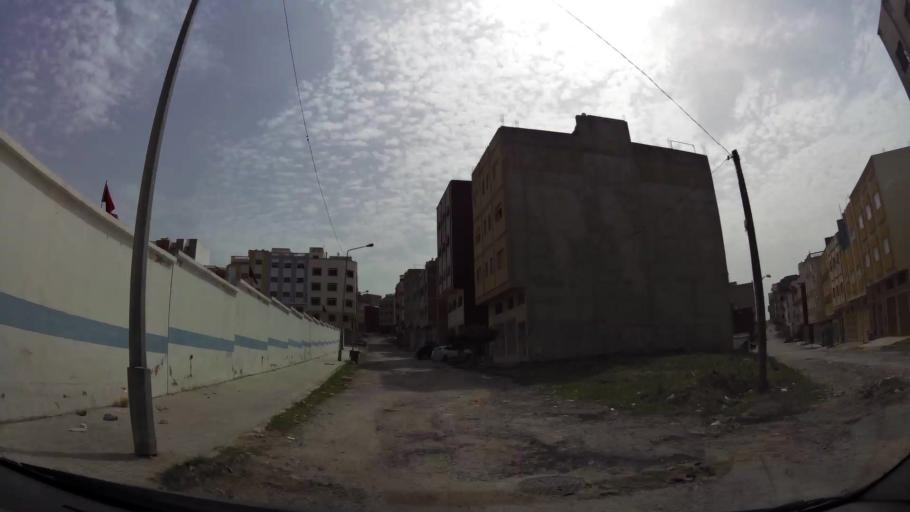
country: MA
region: Tanger-Tetouan
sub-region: Tanger-Assilah
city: Tangier
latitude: 35.7416
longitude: -5.8355
